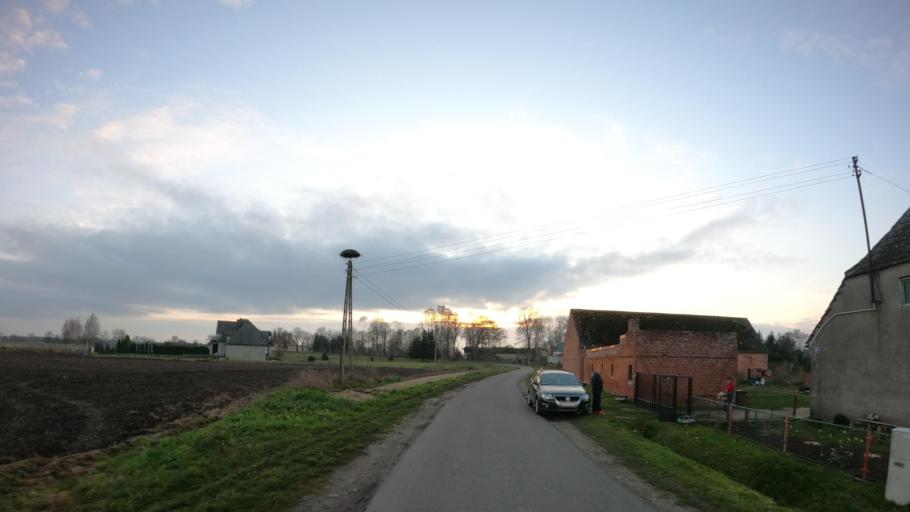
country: PL
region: West Pomeranian Voivodeship
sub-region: Powiat bialogardzki
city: Karlino
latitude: 54.0841
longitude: 15.8830
